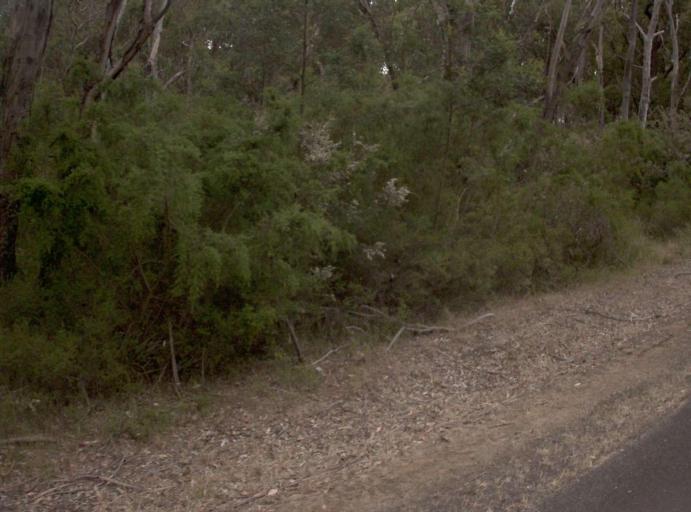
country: AU
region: Victoria
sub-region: Wellington
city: Sale
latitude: -38.3908
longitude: 146.9751
